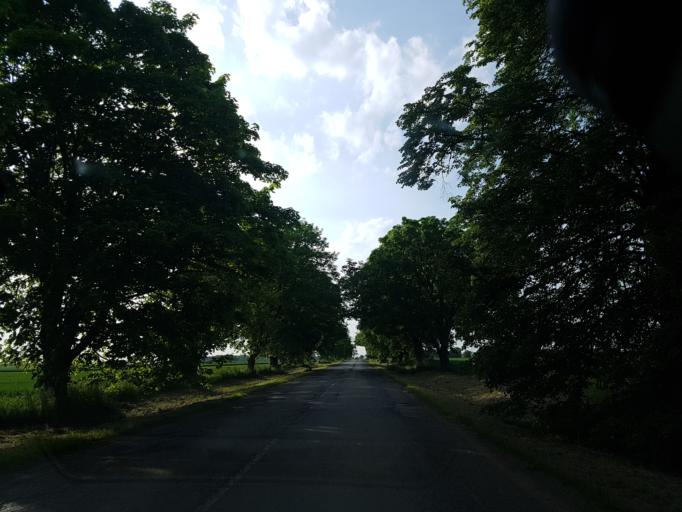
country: PL
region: Lower Silesian Voivodeship
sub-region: Powiat wroclawski
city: Kobierzyce
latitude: 50.9223
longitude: 16.9512
